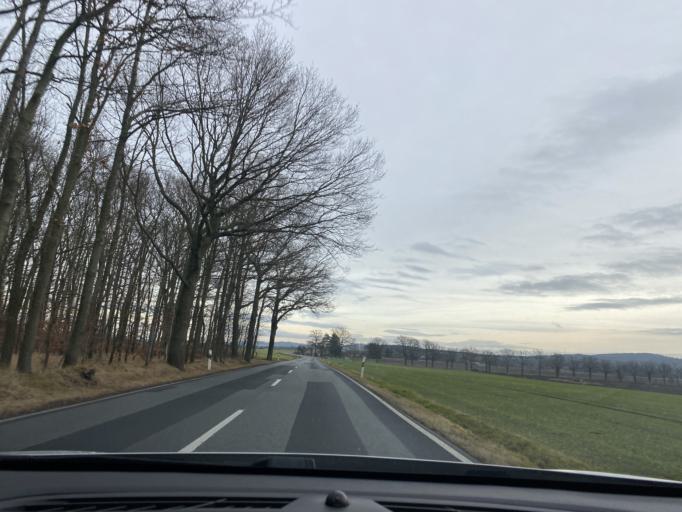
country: DE
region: Saxony
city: Reichenbach
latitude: 51.1234
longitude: 14.8189
